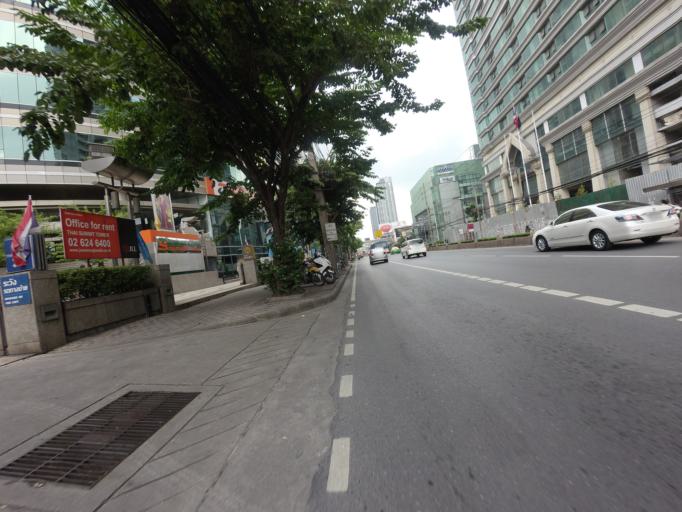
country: TH
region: Bangkok
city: Watthana
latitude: 13.7484
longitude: 100.5676
